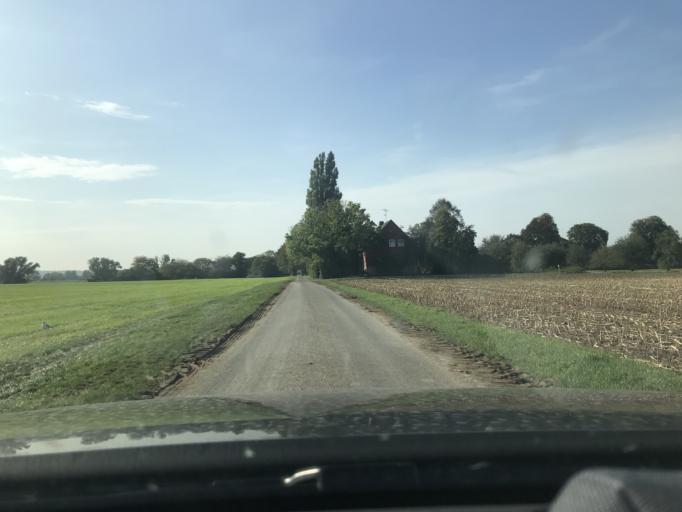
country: DE
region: North Rhine-Westphalia
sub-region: Regierungsbezirk Dusseldorf
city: Emmerich
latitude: 51.8208
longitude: 6.2027
